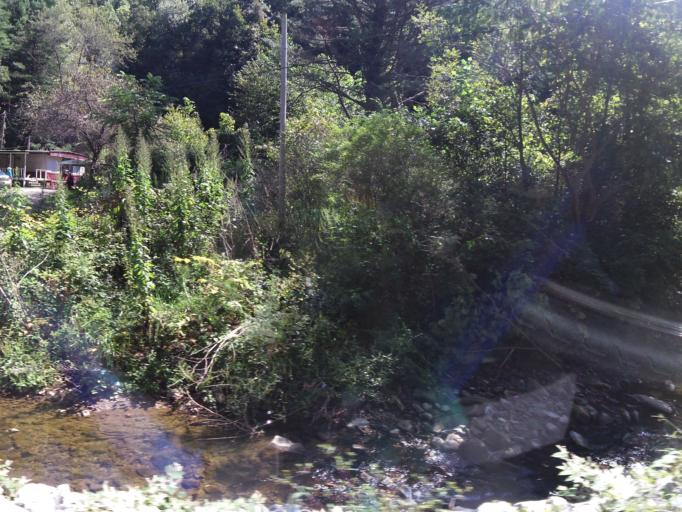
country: US
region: Kentucky
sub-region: Clay County
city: Manchester
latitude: 37.1207
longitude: -83.6381
